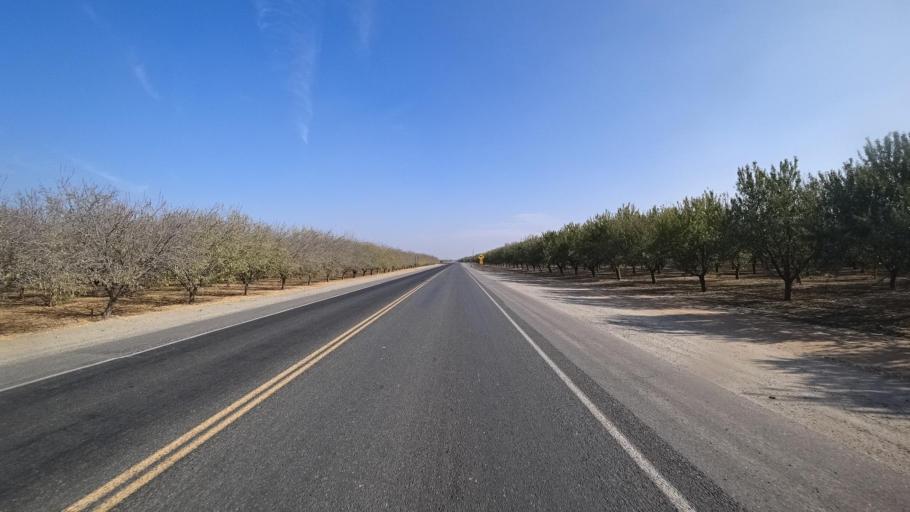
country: US
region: California
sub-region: Kern County
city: McFarland
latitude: 35.6456
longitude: -119.1993
